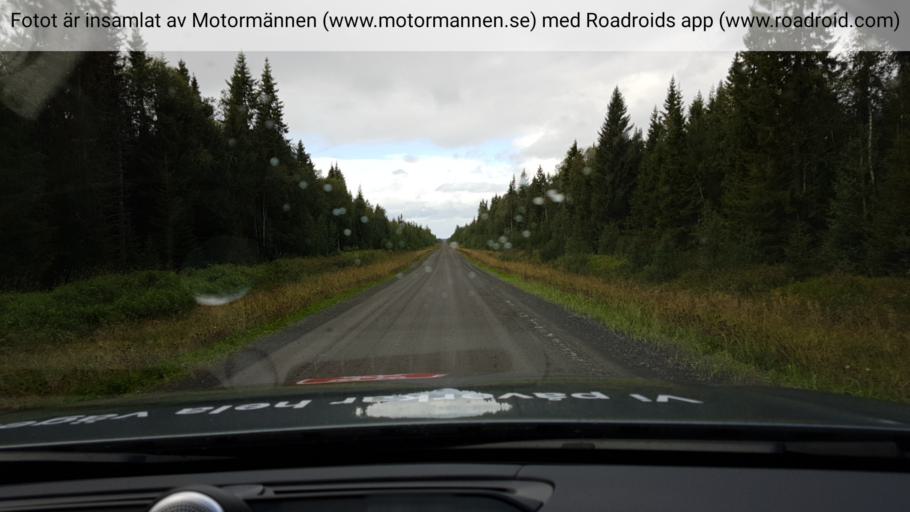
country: SE
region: Jaemtland
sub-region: OEstersunds Kommun
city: Lit
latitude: 63.6563
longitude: 14.9250
